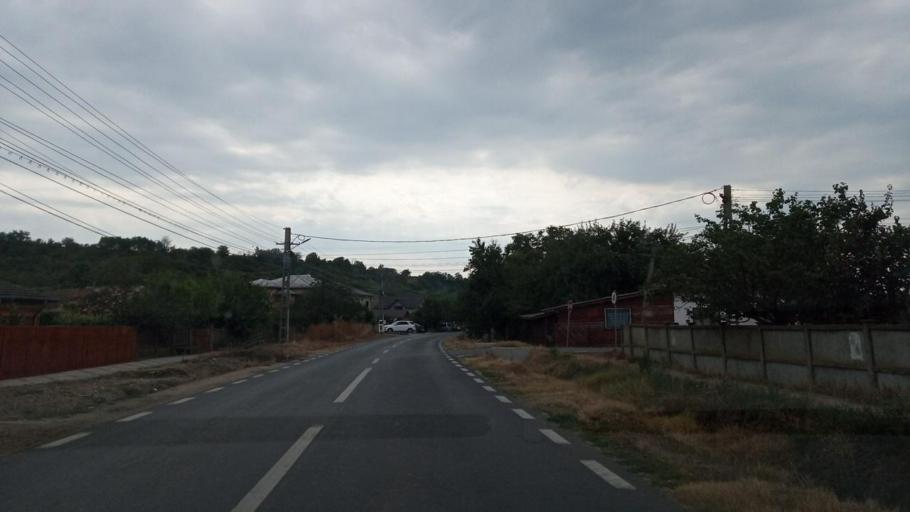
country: RO
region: Giurgiu
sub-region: Comuna Hotarele
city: Hotarele
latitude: 44.1733
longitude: 26.3502
